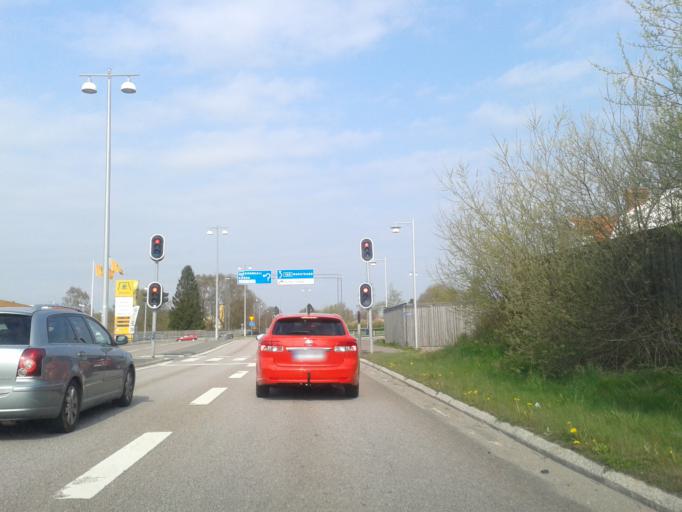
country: SE
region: Vaestra Goetaland
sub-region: Kungalvs Kommun
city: Kungalv
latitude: 57.8647
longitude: 11.9269
